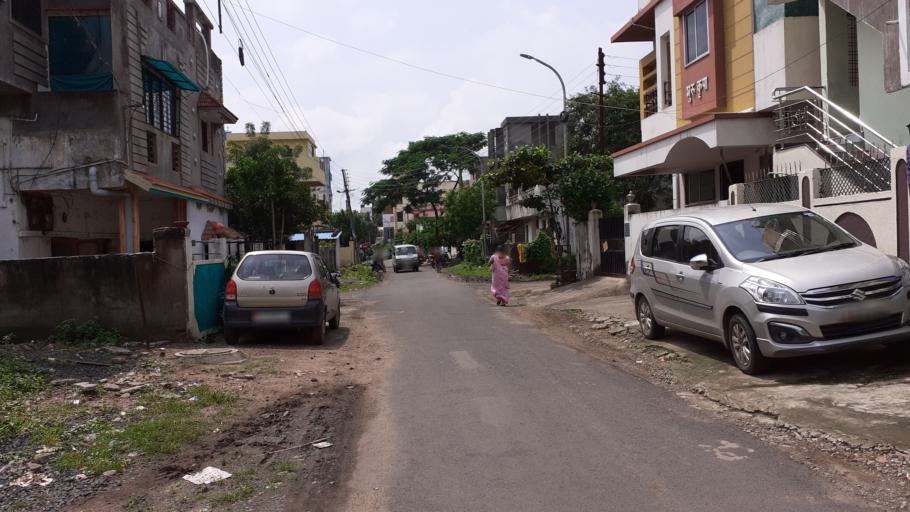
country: IN
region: Maharashtra
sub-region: Nagpur Division
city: Nagpur
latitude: 21.1054
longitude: 79.1145
